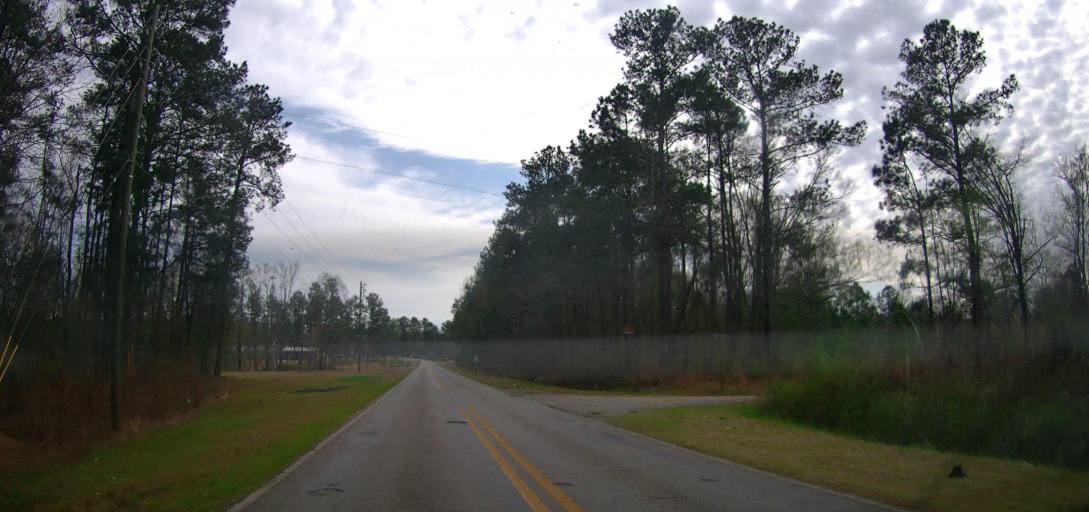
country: US
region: Georgia
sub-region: Jones County
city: Gray
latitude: 32.9814
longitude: -83.6636
